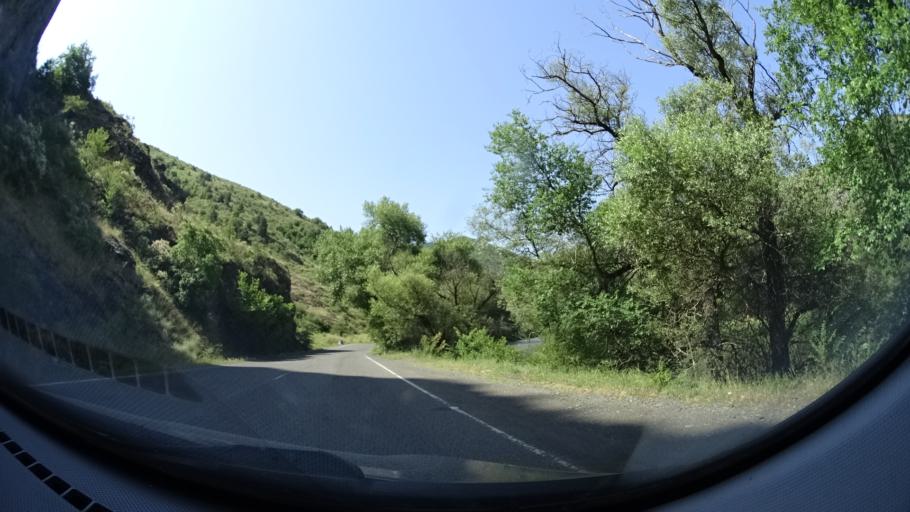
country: GE
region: Samtskhe-Javakheti
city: Akhaltsikhe
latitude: 41.6202
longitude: 43.0691
